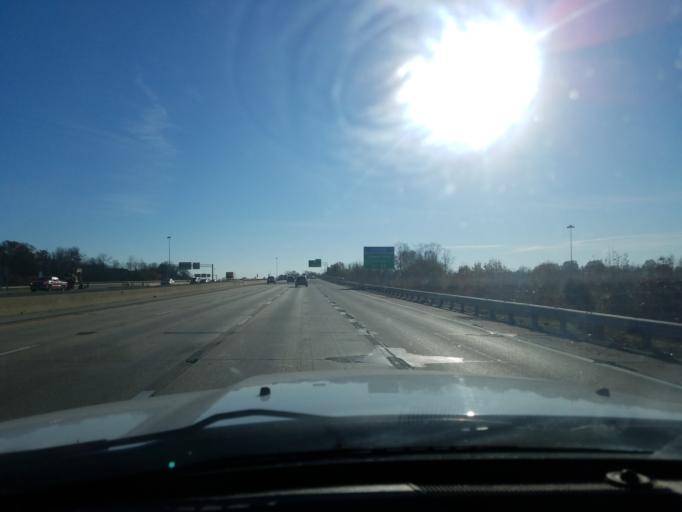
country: US
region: Kentucky
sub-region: Kenton County
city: Crestview Hills
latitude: 39.0292
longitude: -84.5790
